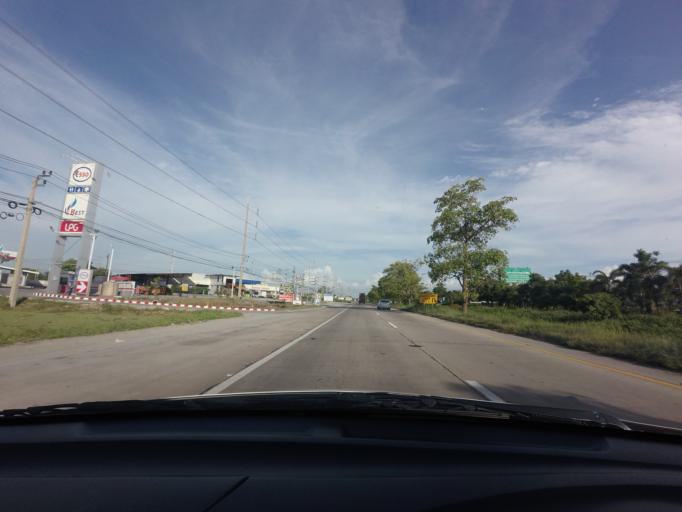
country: TH
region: Phra Nakhon Si Ayutthaya
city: Lat Bua Luang
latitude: 14.0870
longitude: 100.3102
